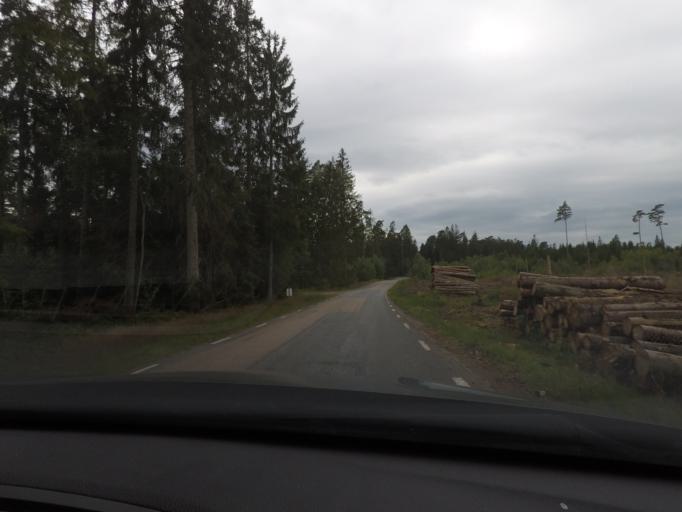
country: SE
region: Kronoberg
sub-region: Markaryds Kommun
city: Stromsnasbruk
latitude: 56.4245
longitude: 13.7482
